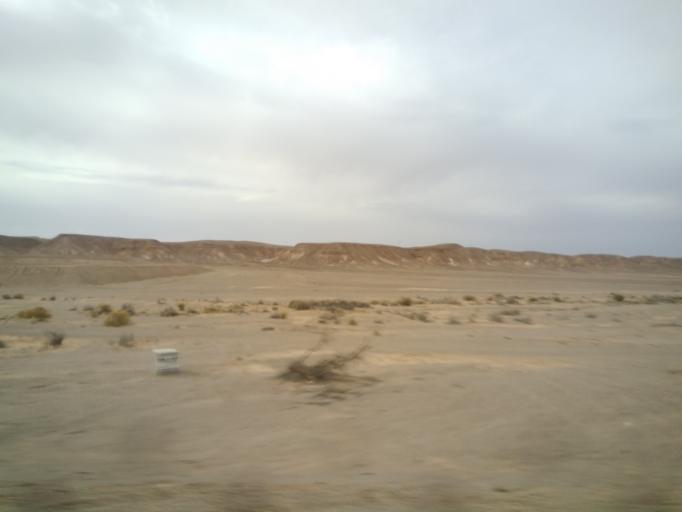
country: IL
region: Southern District
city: Eilat
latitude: 29.9062
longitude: 34.8645
